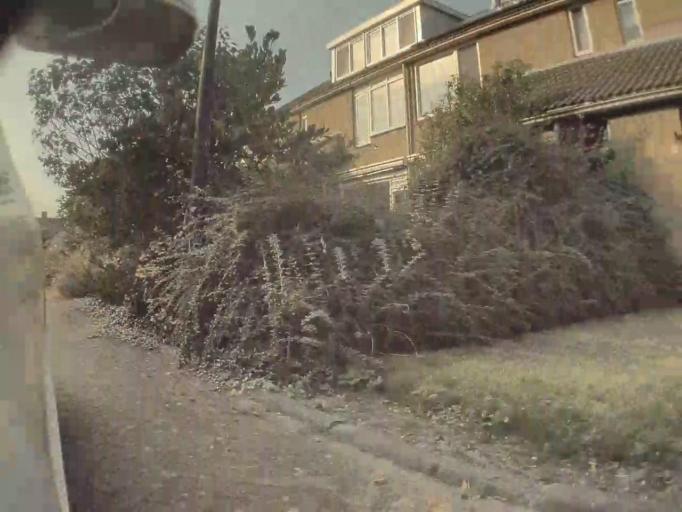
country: NL
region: South Holland
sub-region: Gemeente Teylingen
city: Sassenheim
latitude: 52.2137
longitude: 4.5601
